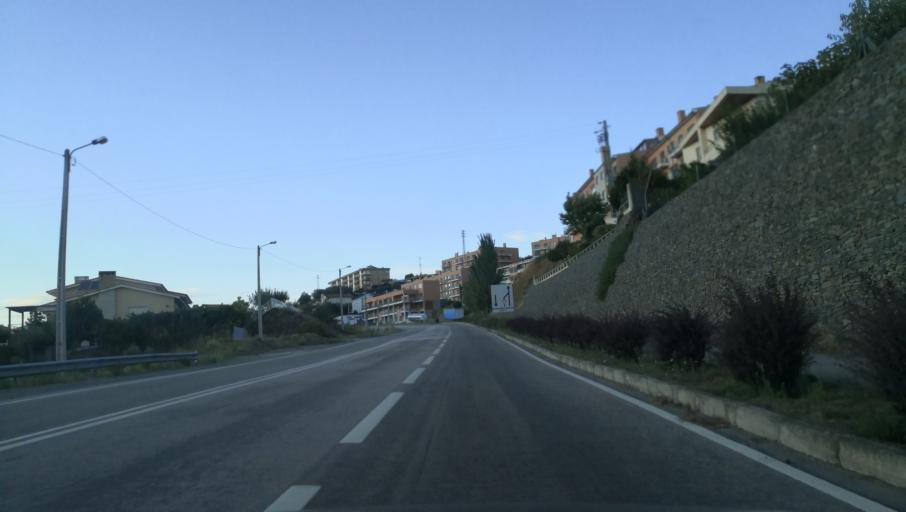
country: PT
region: Vila Real
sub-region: Peso da Regua
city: Peso da Regua
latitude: 41.1597
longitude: -7.7803
